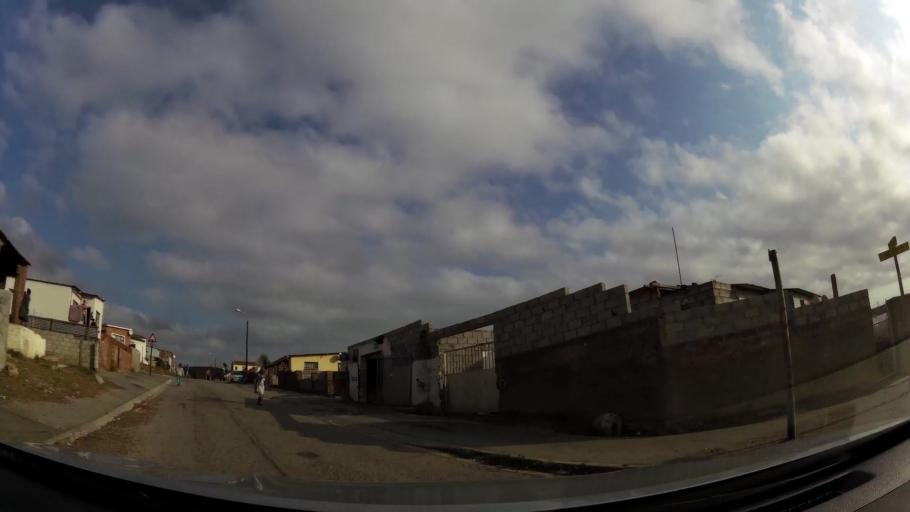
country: ZA
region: Eastern Cape
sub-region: Nelson Mandela Bay Metropolitan Municipality
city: Port Elizabeth
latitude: -33.9177
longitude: 25.5477
